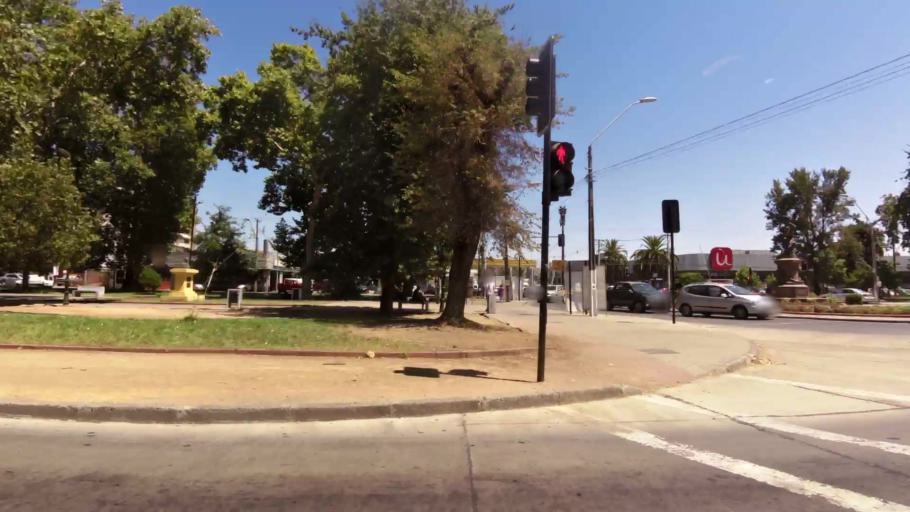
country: CL
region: Maule
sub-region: Provincia de Curico
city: Curico
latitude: -34.9856
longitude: -71.2338
